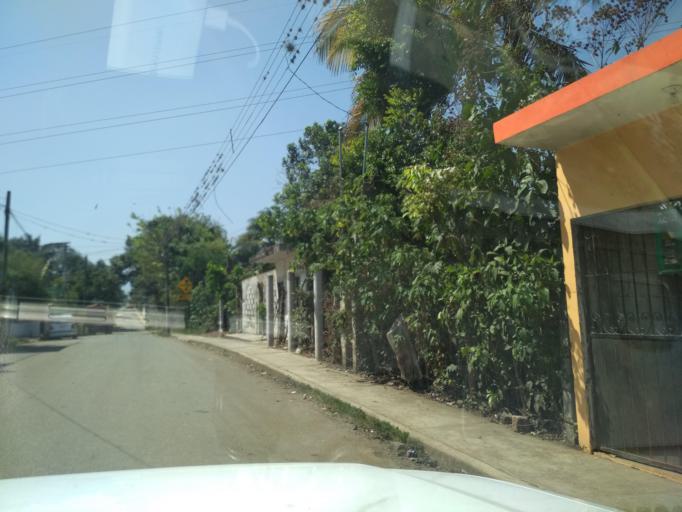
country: MX
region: Veracruz
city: Amatlan de los Reyes
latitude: 18.8536
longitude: -96.9198
